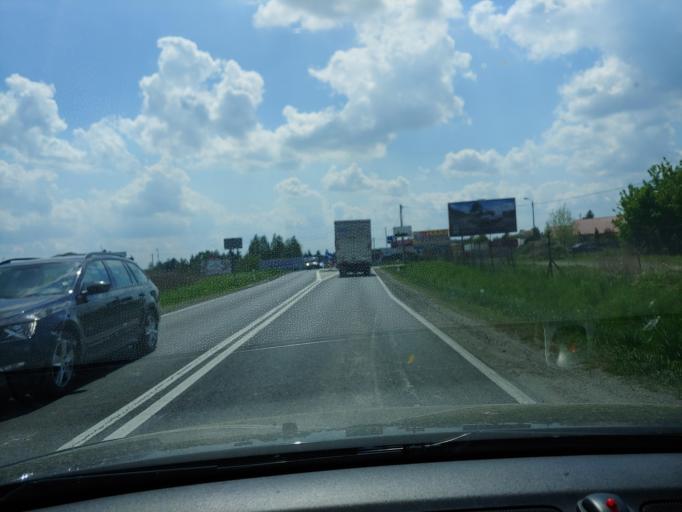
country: PL
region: Lesser Poland Voivodeship
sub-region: Powiat tarnowski
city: Lisia Gora
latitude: 50.0713
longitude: 21.0188
